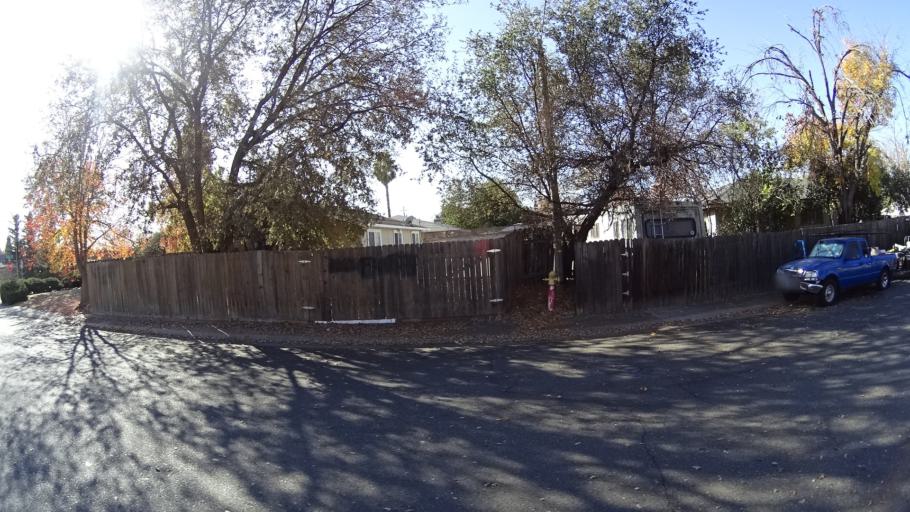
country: US
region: California
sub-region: Sacramento County
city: Antelope
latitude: 38.6867
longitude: -121.3102
